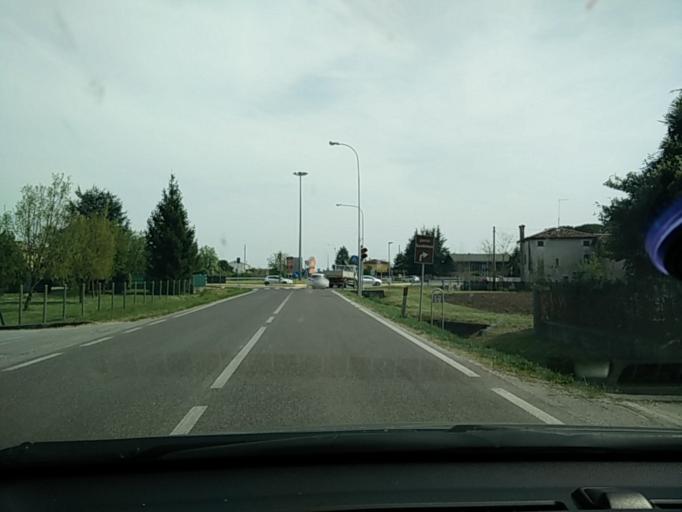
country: IT
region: Veneto
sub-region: Provincia di Treviso
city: Codogne
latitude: 45.8604
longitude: 12.4112
